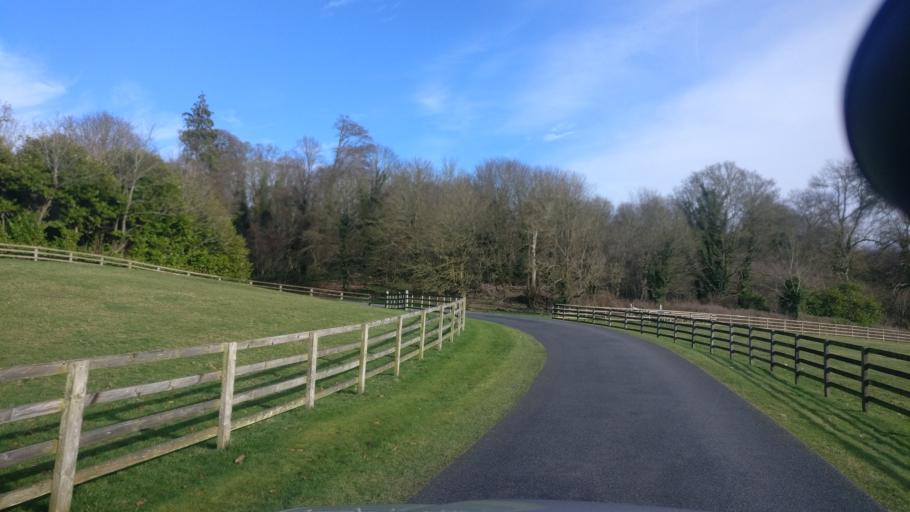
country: IE
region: Leinster
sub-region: Kilkenny
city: Thomastown
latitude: 52.5325
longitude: -7.1830
